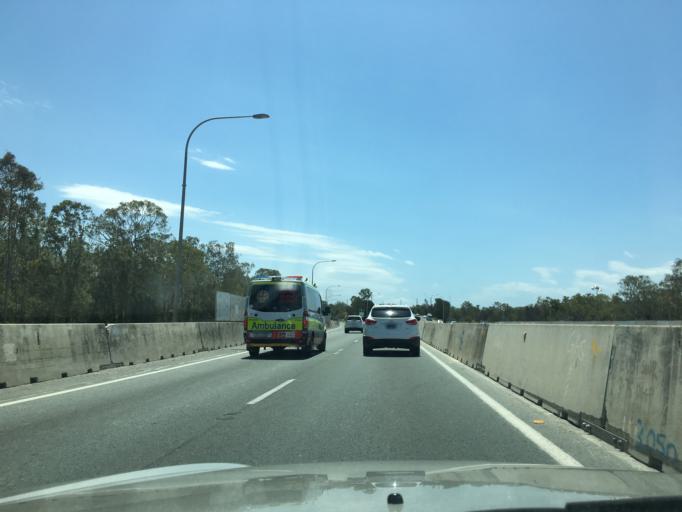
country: AU
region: Queensland
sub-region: Brisbane
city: Deagon
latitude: -27.3459
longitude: 153.0770
